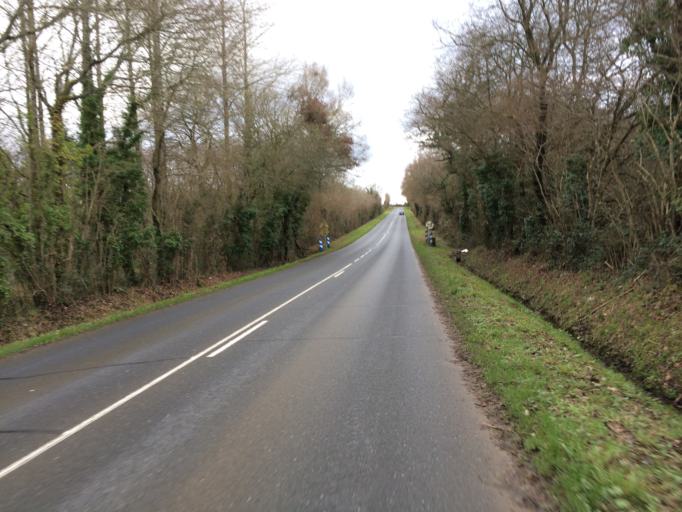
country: FR
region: Brittany
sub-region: Departement du Finistere
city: Daoulas
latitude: 48.3418
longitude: -4.2593
